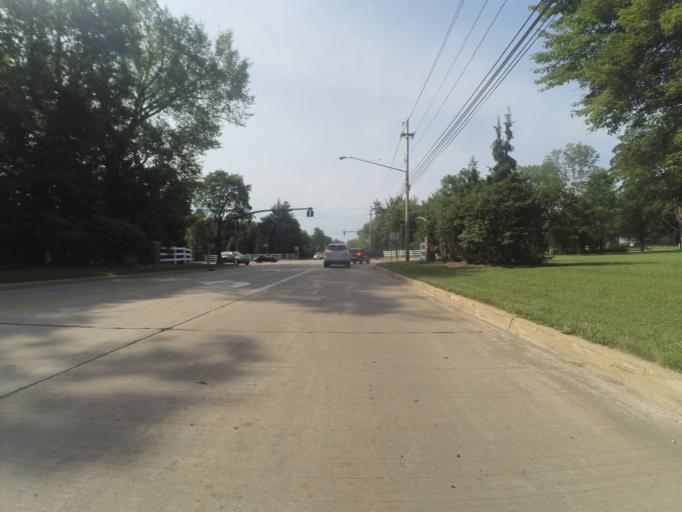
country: US
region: Ohio
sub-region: Cuyahoga County
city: Orange
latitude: 41.4499
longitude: -81.4803
